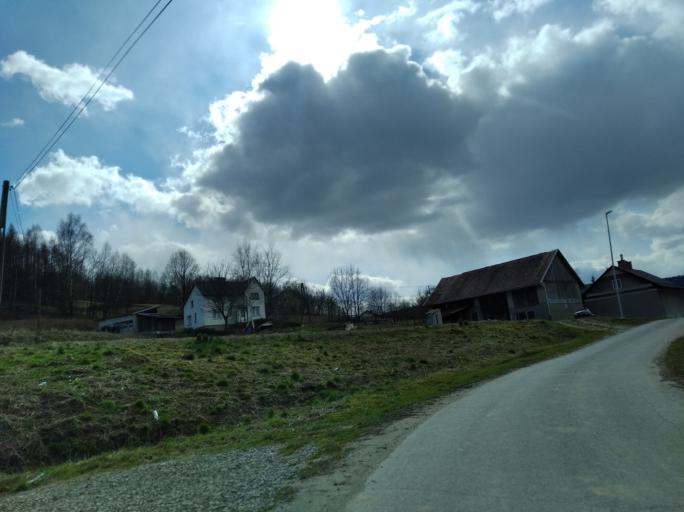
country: PL
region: Subcarpathian Voivodeship
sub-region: Powiat strzyzowski
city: Strzyzow
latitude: 49.8321
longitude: 21.8365
